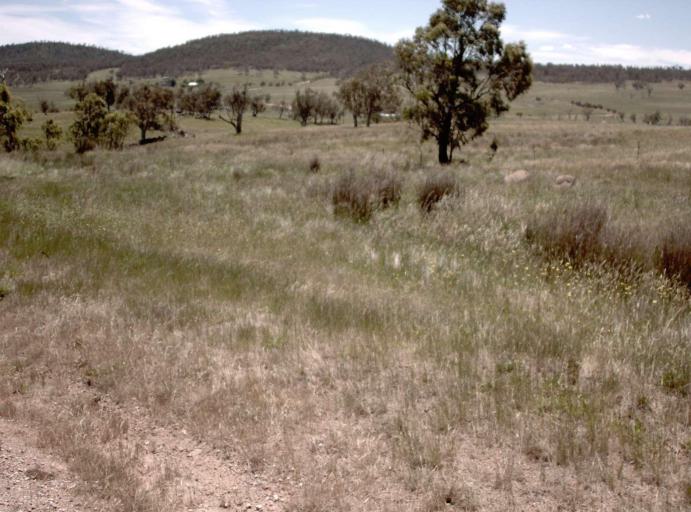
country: AU
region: New South Wales
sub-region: Snowy River
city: Jindabyne
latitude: -37.0176
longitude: 148.2740
